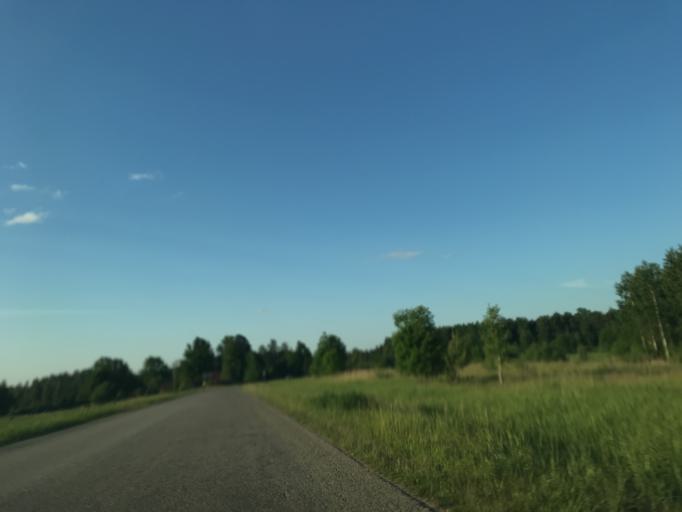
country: LV
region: Baldone
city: Baldone
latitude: 56.7120
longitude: 24.3682
